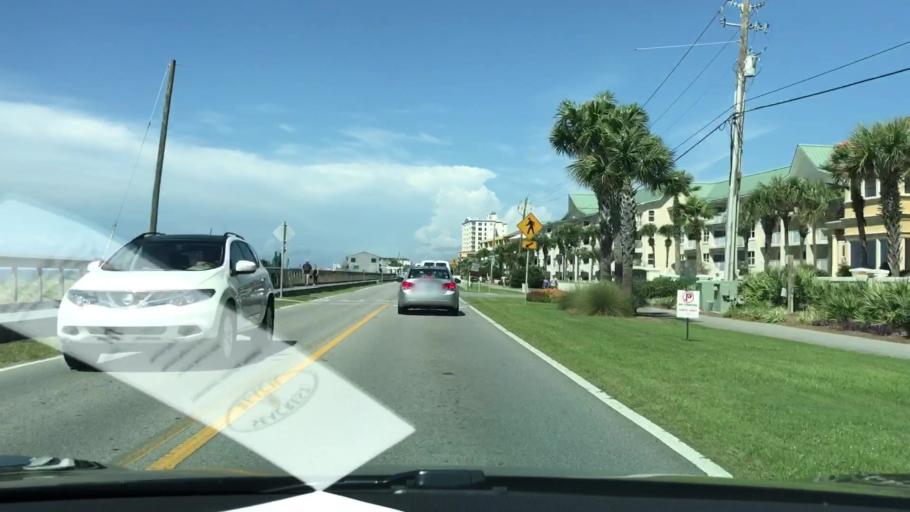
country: US
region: Florida
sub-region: Walton County
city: Miramar Beach
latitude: 30.3784
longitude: -86.3901
